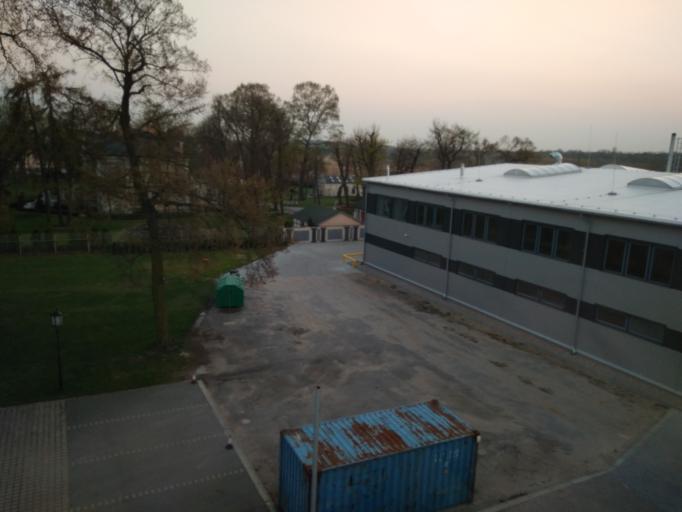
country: PL
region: Greater Poland Voivodeship
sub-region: Powiat gnieznienski
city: Gniezno
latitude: 52.5254
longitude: 17.5960
